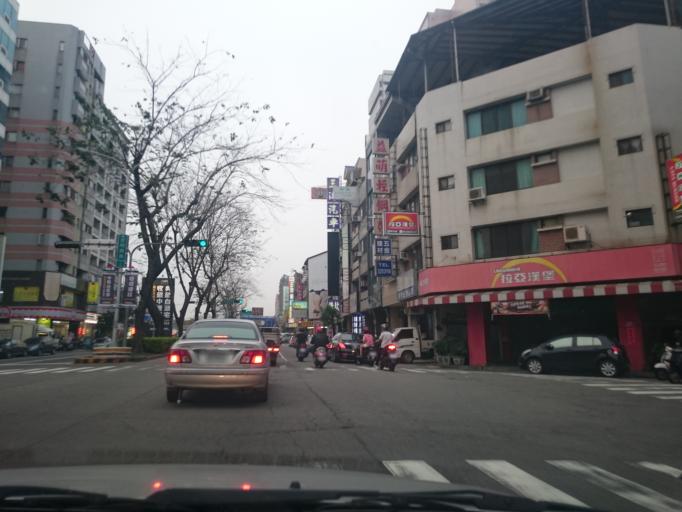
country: TW
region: Taiwan
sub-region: Taichung City
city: Taichung
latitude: 24.1554
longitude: 120.6586
